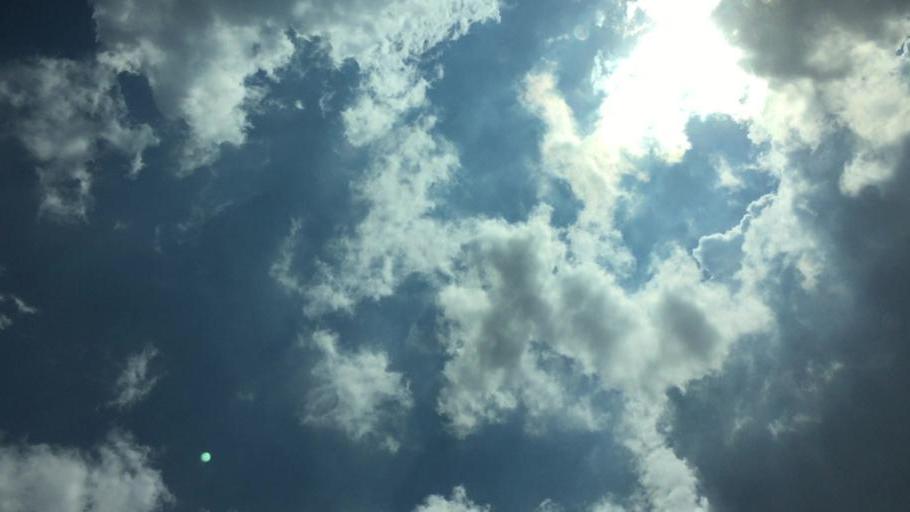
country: US
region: Georgia
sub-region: DeKalb County
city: Druid Hills
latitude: 33.7912
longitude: -84.3684
